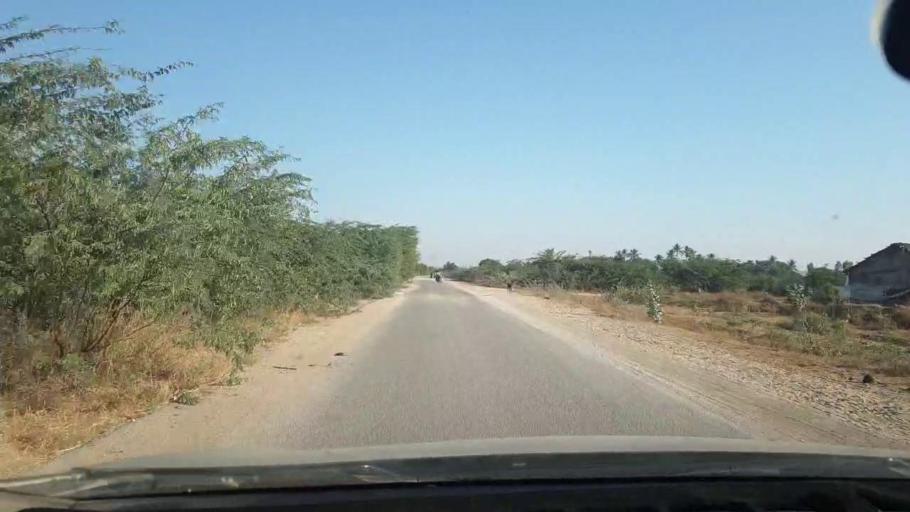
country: PK
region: Sindh
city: Malir Cantonment
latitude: 25.1717
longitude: 67.2014
